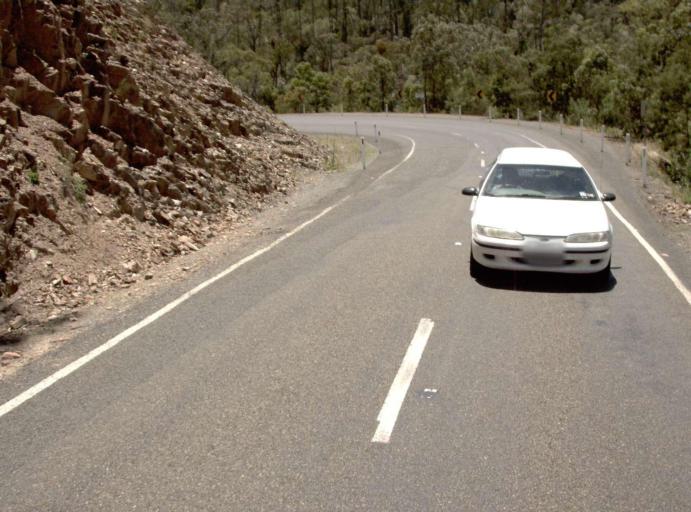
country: AU
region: Victoria
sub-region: East Gippsland
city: Bairnsdale
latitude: -37.4754
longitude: 147.8327
